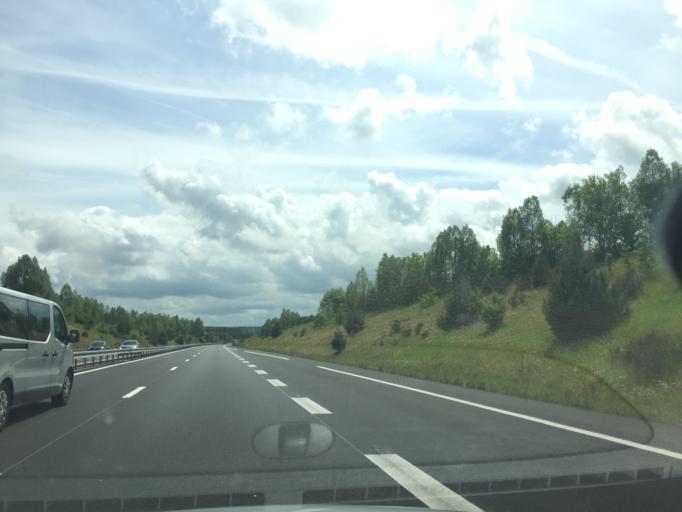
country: FR
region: Pays de la Loire
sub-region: Departement de la Sarthe
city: Marigne-Laille
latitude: 47.8176
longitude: 0.3072
